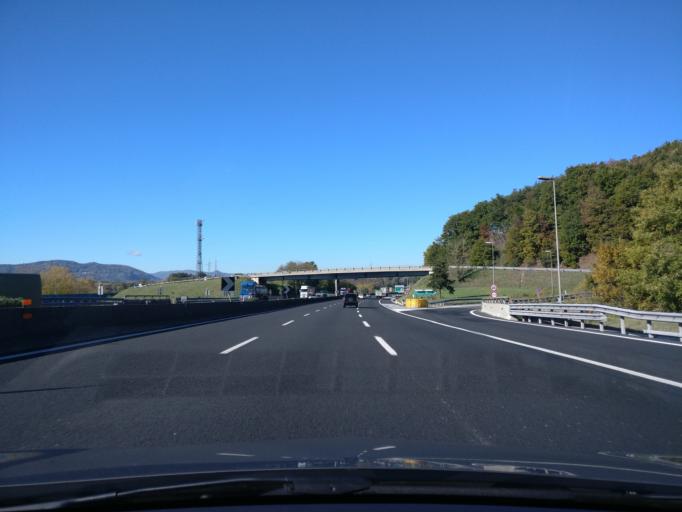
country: IT
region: Latium
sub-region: Citta metropolitana di Roma Capitale
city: Colleferro
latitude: 41.7493
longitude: 12.9936
